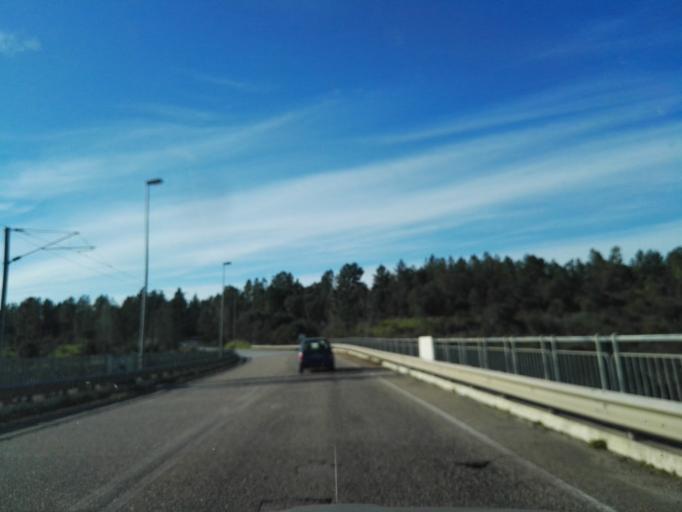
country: PT
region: Santarem
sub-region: Abrantes
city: Alferrarede
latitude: 39.4717
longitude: -8.0672
